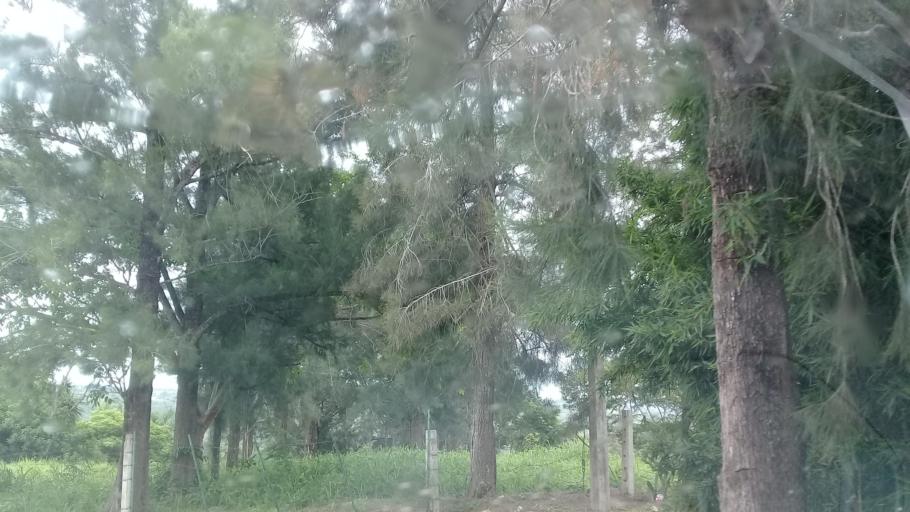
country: MX
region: Veracruz
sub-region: Emiliano Zapata
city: Jacarandas
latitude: 19.5097
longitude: -96.8382
